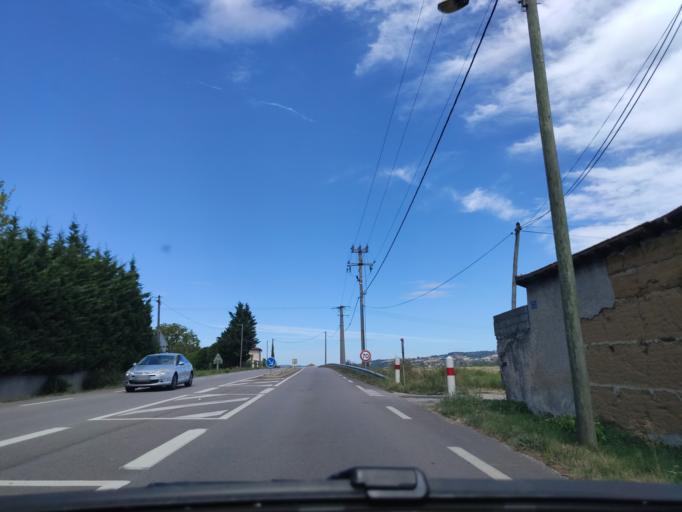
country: FR
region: Rhone-Alpes
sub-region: Departement de l'Isere
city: Auberives-sur-Vareze
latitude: 45.4379
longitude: 4.8196
